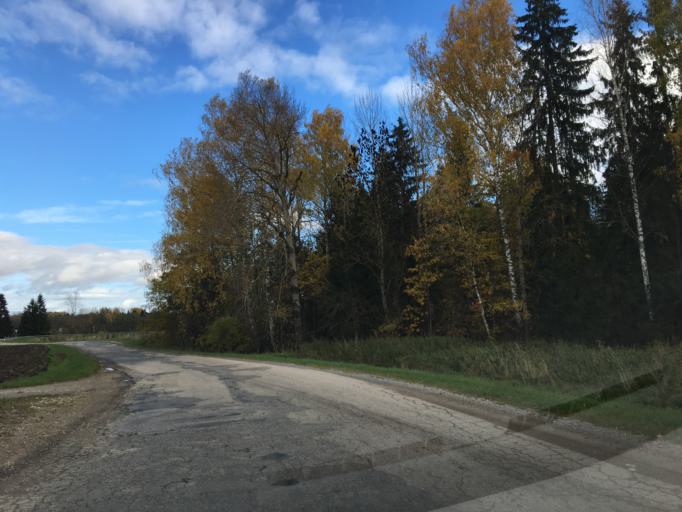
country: EE
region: Tartu
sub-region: Puhja vald
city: Puhja
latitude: 58.4672
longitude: 26.3659
